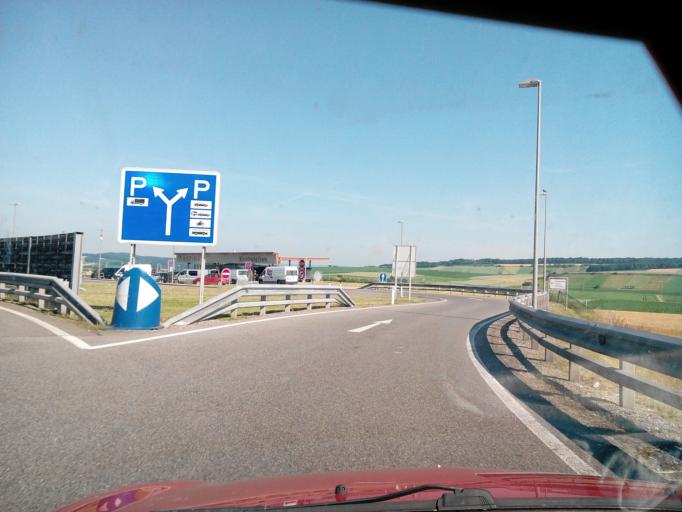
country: AT
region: Lower Austria
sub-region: Politischer Bezirk Sankt Polten
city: Kirchstetten
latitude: 48.1854
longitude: 15.7994
